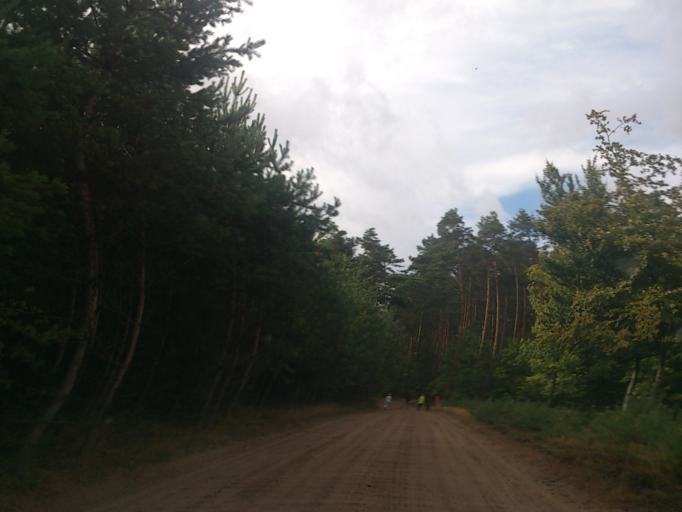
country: PL
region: Greater Poland Voivodeship
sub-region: Powiat poznanski
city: Kobylnica
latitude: 52.5238
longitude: 17.1268
